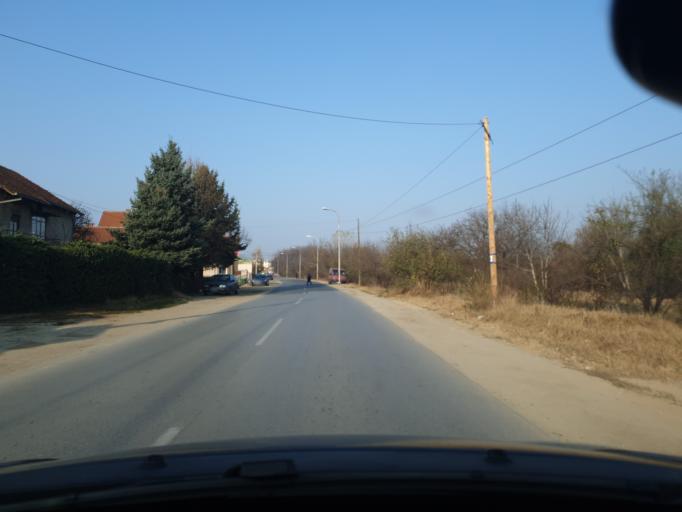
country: RS
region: Central Serbia
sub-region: Jablanicki Okrug
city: Leskovac
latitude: 42.9957
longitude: 21.9284
